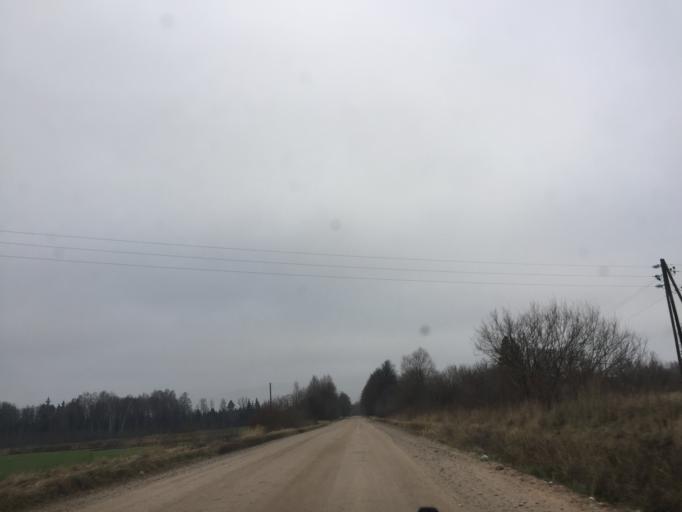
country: LV
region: Limbazu Rajons
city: Limbazi
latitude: 57.5822
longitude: 24.5136
